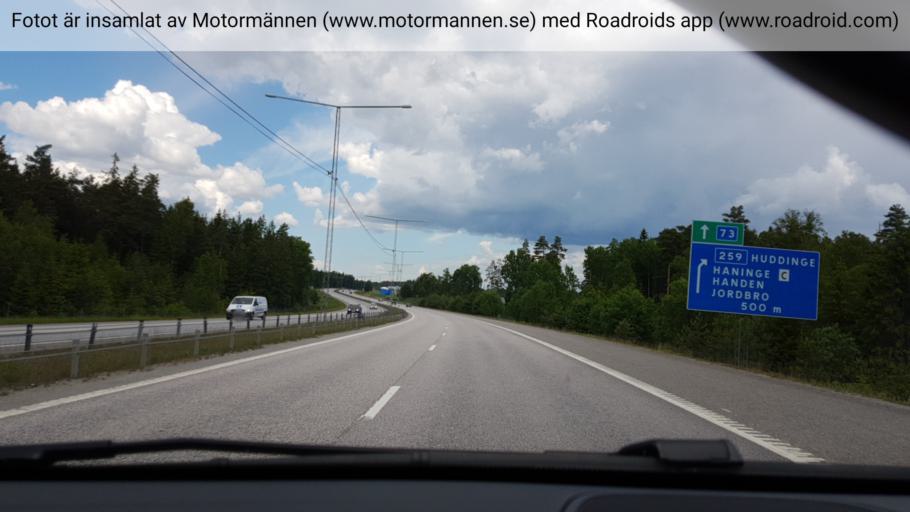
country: SE
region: Stockholm
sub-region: Haninge Kommun
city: Haninge
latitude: 59.1432
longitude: 18.1611
